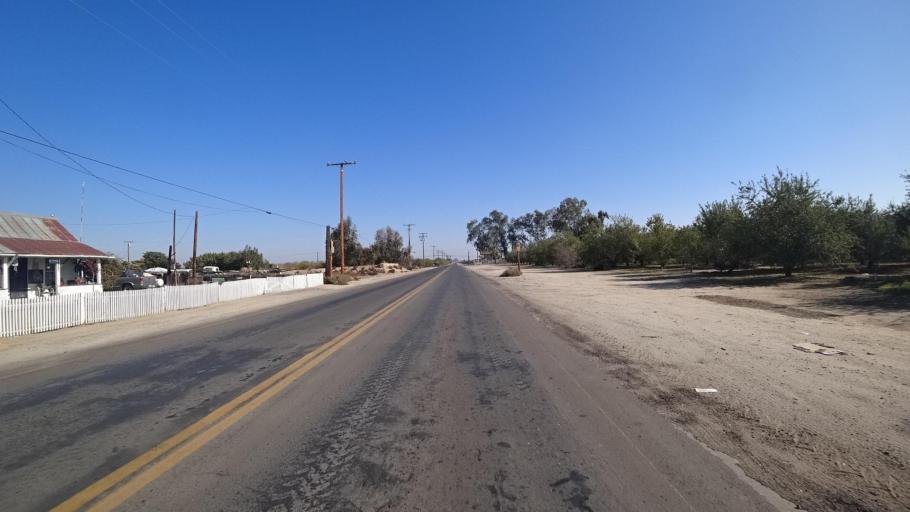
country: US
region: California
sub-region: Kern County
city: McFarland
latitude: 35.6889
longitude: -119.2254
